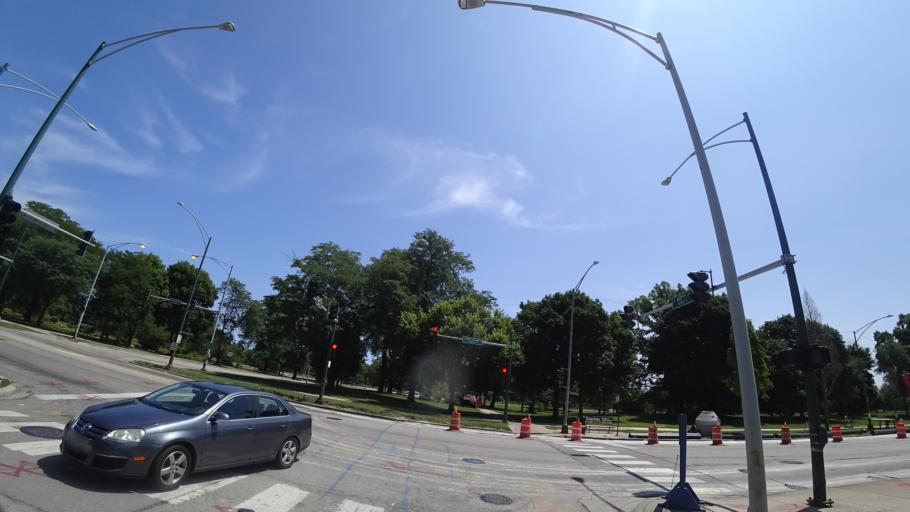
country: US
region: Illinois
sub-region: Cook County
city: Chicago
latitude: 41.7861
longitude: -87.5868
